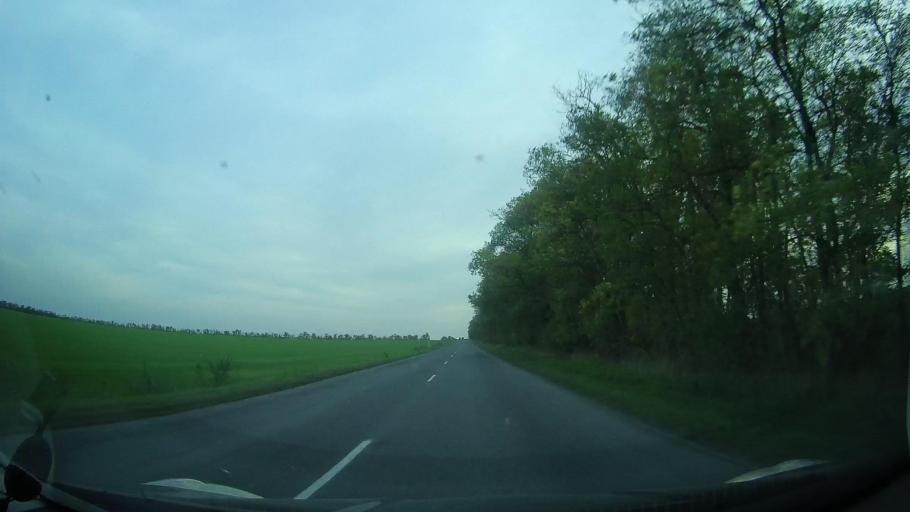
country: RU
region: Rostov
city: Kirovskaya
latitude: 47.0458
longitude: 39.9770
